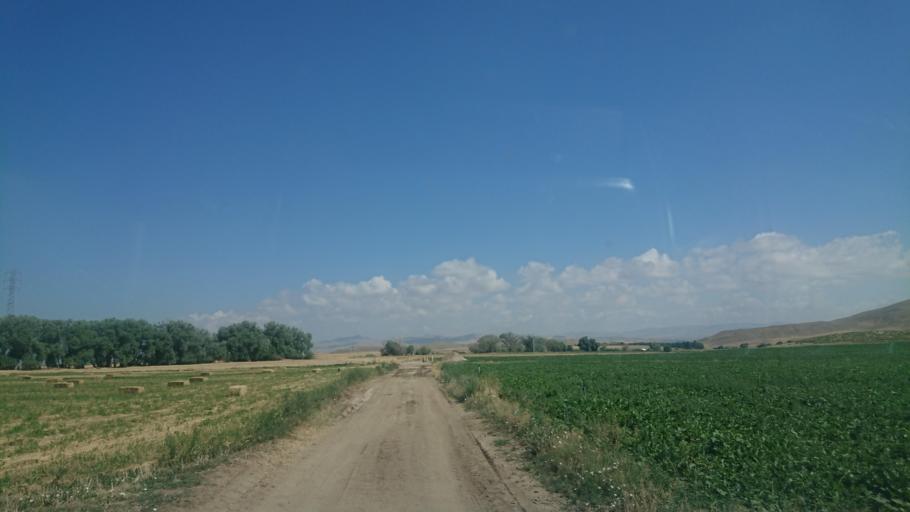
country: TR
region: Aksaray
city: Sariyahsi
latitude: 38.9952
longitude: 33.8952
